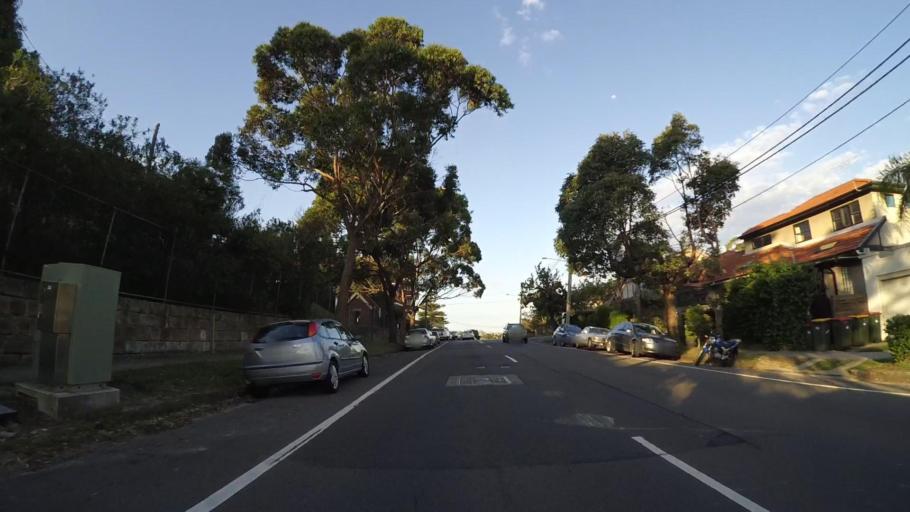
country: AU
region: New South Wales
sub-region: Randwick
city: Randwick
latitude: -33.9223
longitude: 151.2460
